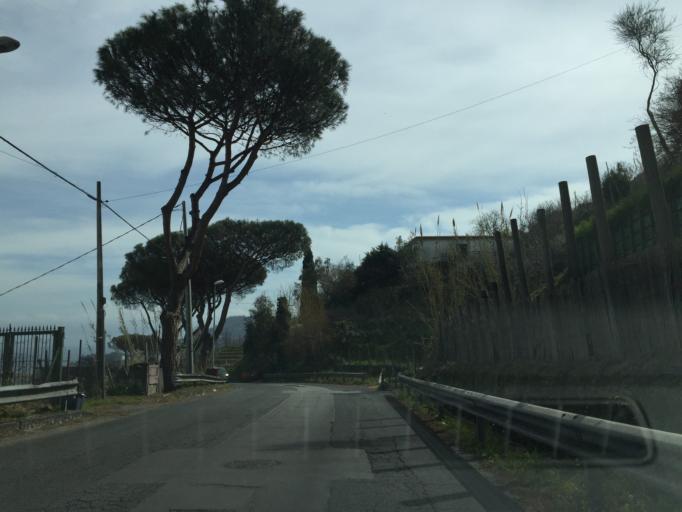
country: IT
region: Campania
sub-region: Provincia di Napoli
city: Monte di Procida
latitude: 40.7953
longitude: 14.0605
